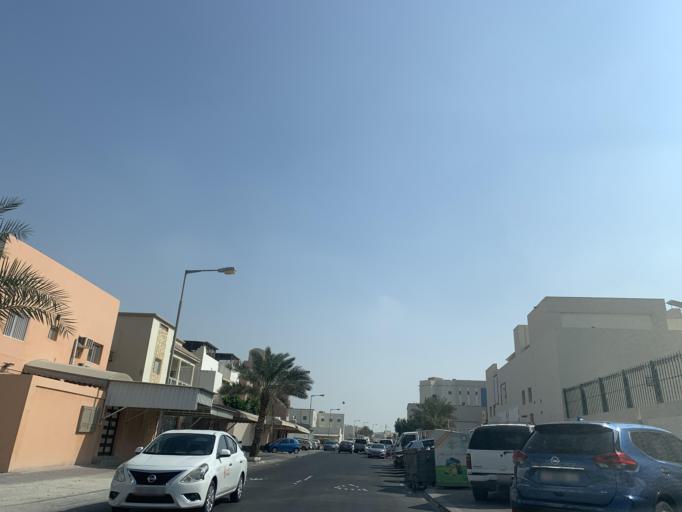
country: BH
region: Central Governorate
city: Madinat Hamad
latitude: 26.1253
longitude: 50.4937
